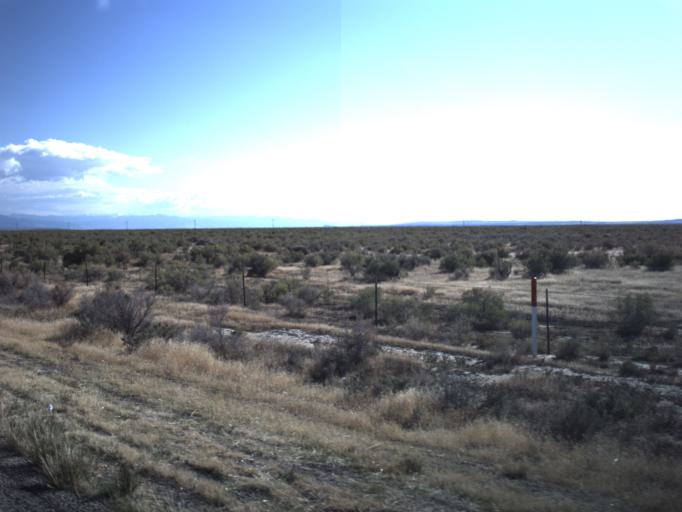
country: US
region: Utah
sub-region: Millard County
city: Delta
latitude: 39.2483
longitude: -112.4380
